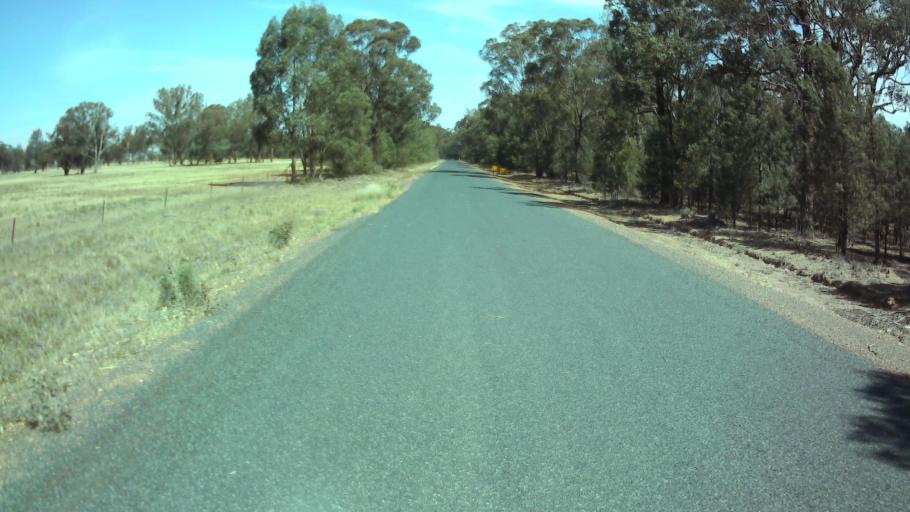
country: AU
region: New South Wales
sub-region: Weddin
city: Grenfell
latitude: -34.0669
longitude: 148.1371
